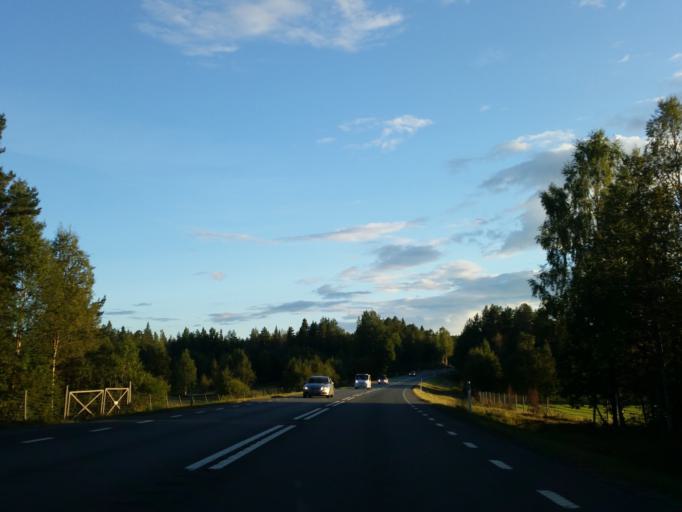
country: SE
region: Vaesterbotten
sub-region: Robertsfors Kommun
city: Robertsfors
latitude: 64.0228
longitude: 20.8398
